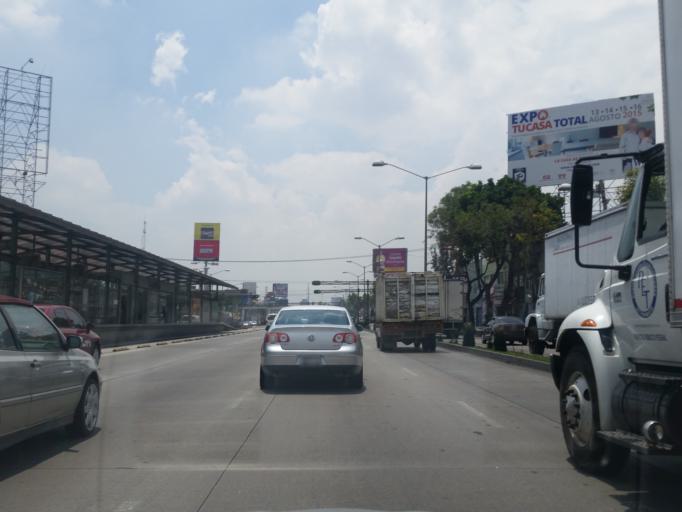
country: MX
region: Mexico City
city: Cuauhtemoc
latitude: 19.4715
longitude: -99.1453
